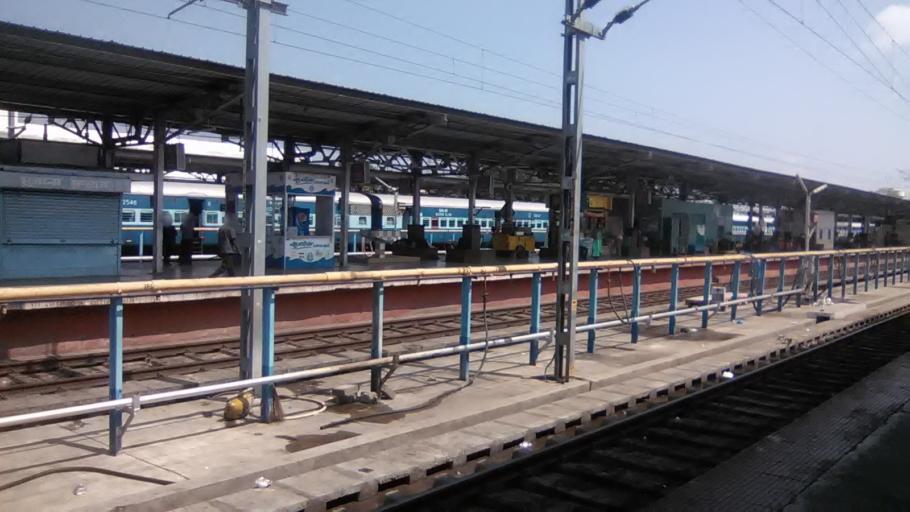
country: IN
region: Tamil Nadu
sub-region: Tiruchchirappalli
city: Tiruchirappalli
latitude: 10.7937
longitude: 78.6858
